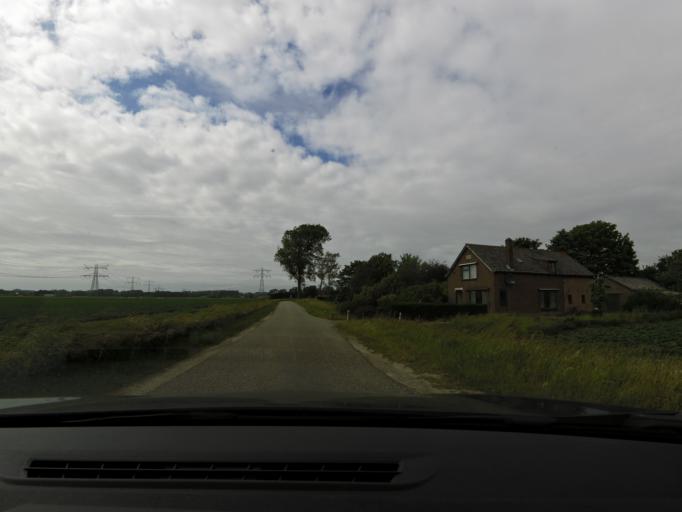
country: NL
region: South Holland
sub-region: Gemeente Brielle
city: Brielle
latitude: 51.9110
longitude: 4.1325
